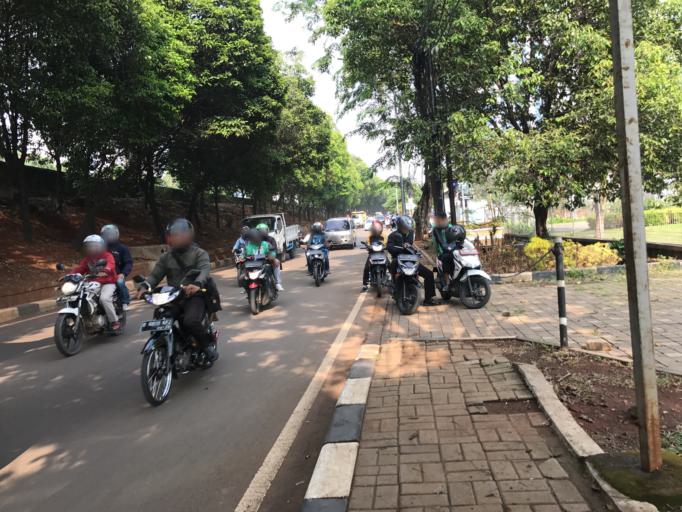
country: ID
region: Jakarta Raya
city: Jakarta
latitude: -6.2919
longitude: 106.8105
